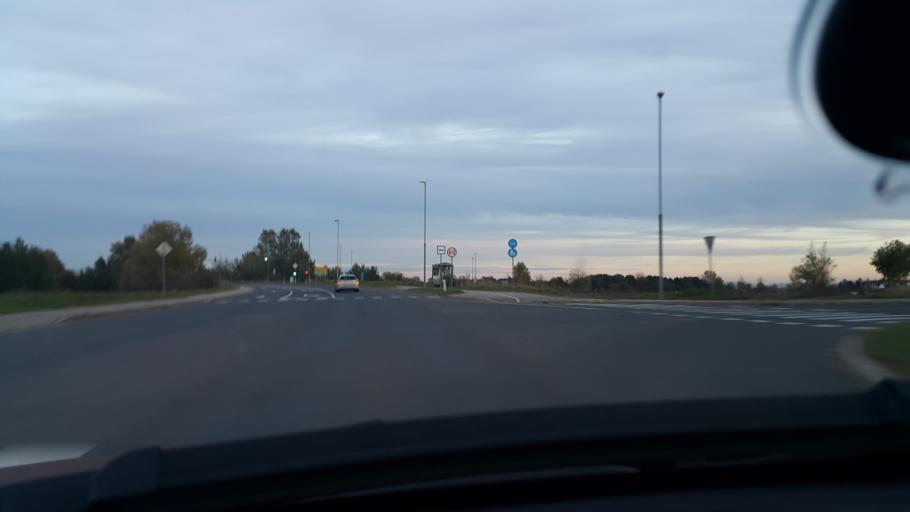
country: SI
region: Hoce-Slivnica
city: Spodnje Hoce
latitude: 46.5011
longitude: 15.6665
